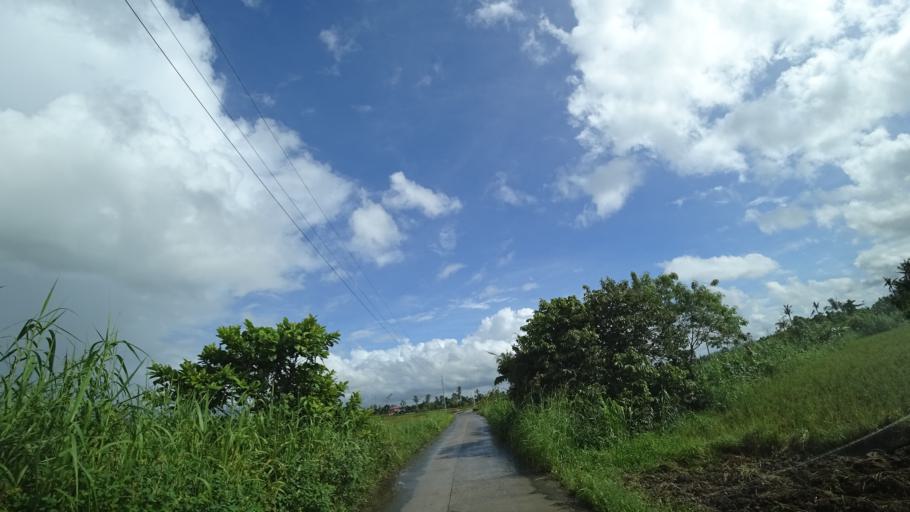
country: PH
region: Eastern Visayas
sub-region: Province of Leyte
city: Mayorga
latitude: 10.9086
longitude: 124.9782
